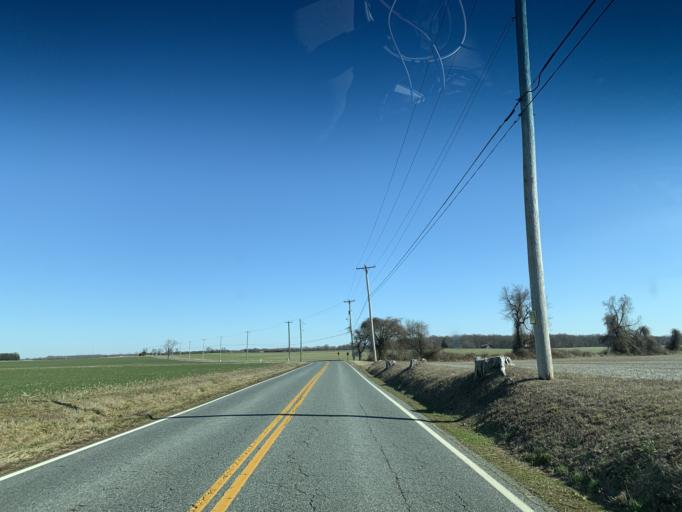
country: US
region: Maryland
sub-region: Cecil County
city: Elkton
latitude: 39.4892
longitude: -75.8727
